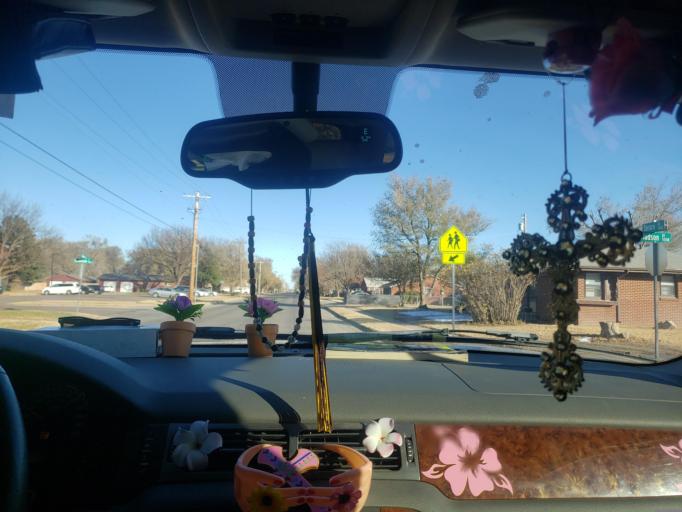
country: US
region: Kansas
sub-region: Finney County
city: Garden City
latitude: 37.9677
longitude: -100.8612
